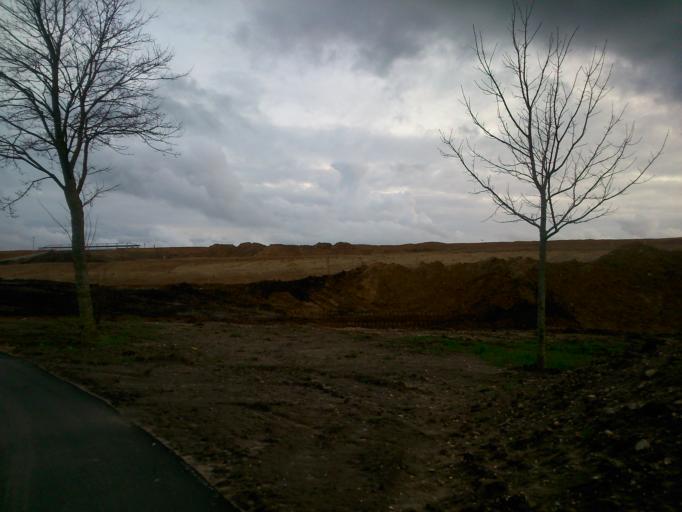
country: DK
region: Central Jutland
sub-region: Holstebro Kommune
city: Holstebro
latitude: 56.3697
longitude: 8.7198
